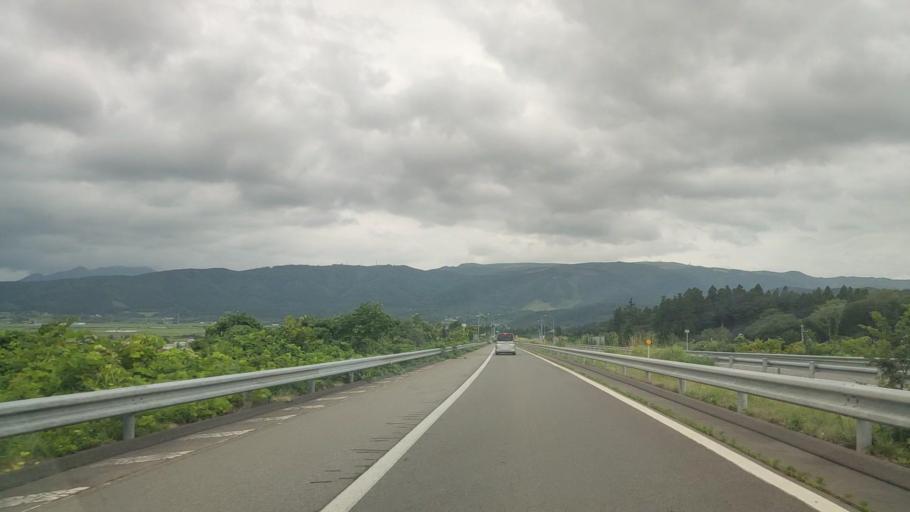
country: JP
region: Hokkaido
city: Nanae
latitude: 41.9209
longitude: 140.6776
